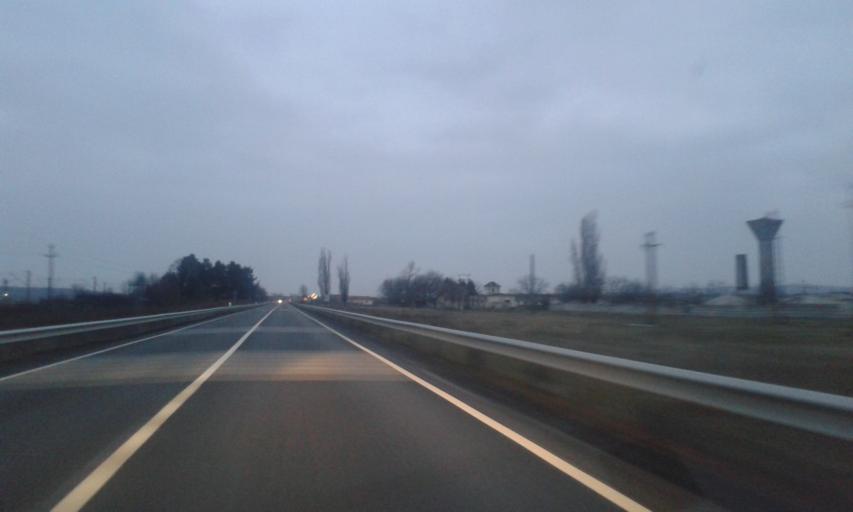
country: RO
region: Gorj
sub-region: Comuna Turcinesti
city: Turcinesti
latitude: 45.1137
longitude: 23.3442
